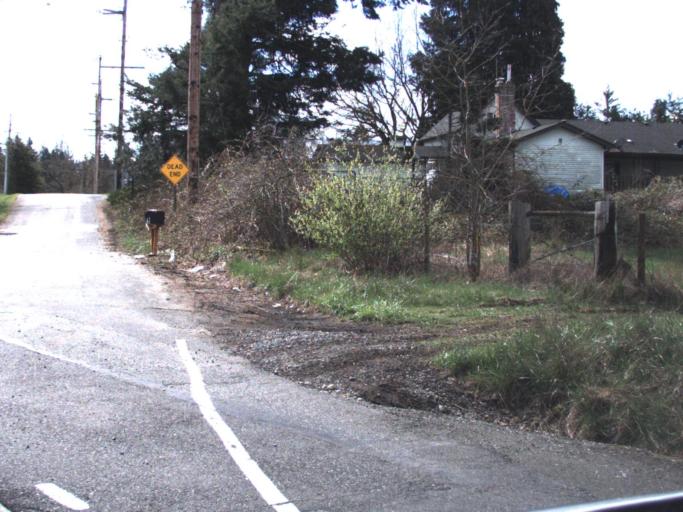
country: US
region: Washington
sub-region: Pierce County
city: Buckley
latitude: 47.2266
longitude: -122.1015
